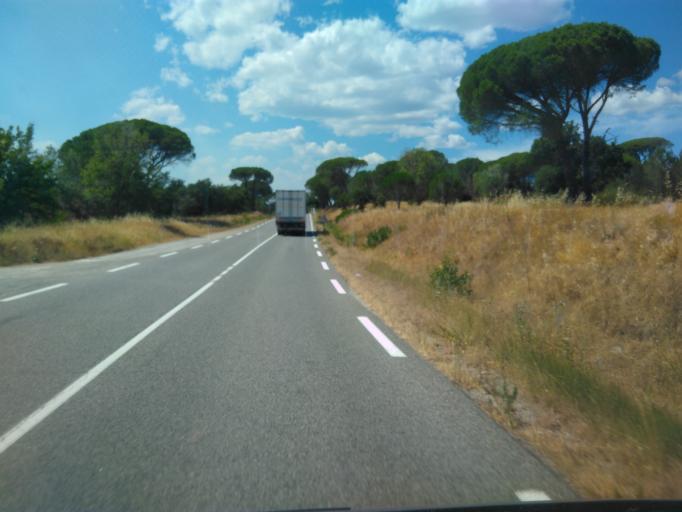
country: FR
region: Provence-Alpes-Cote d'Azur
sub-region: Departement du Var
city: Le Cannet-des-Maures
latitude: 43.3599
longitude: 6.3914
